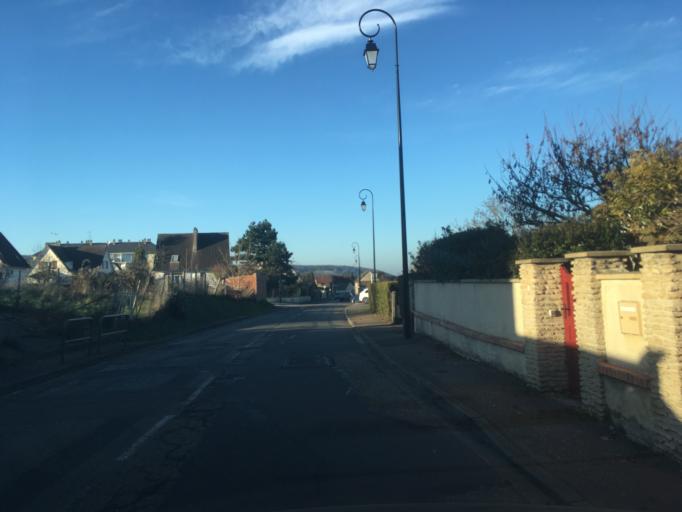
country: FR
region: Haute-Normandie
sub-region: Departement de l'Eure
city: Vernon
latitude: 49.0925
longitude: 1.4557
